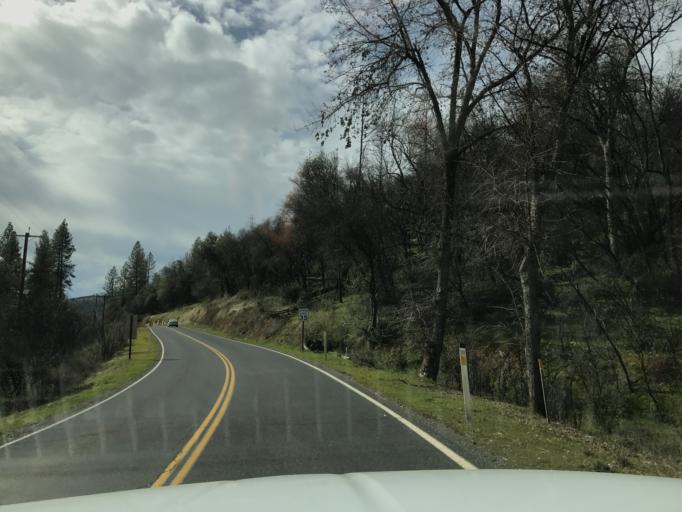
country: US
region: California
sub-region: Calaveras County
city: Mountain Ranch
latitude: 38.2319
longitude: -120.5356
